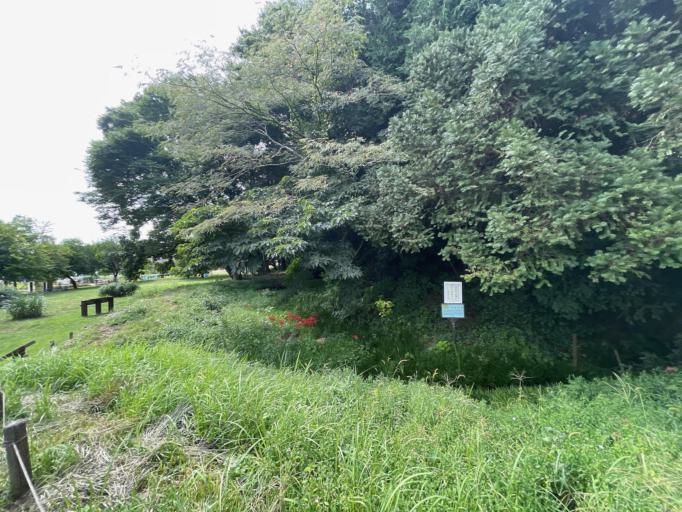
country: JP
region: Saitama
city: Hanno
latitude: 35.8479
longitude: 139.3530
